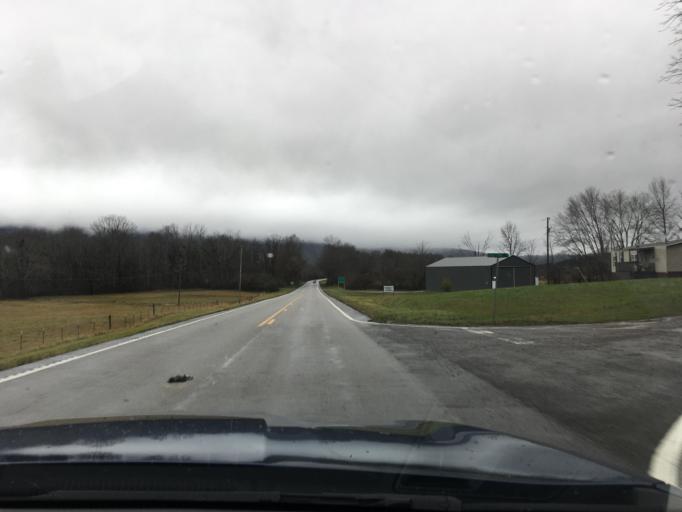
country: US
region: Tennessee
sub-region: Rhea County
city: Spring City
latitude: 35.8294
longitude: -84.9107
